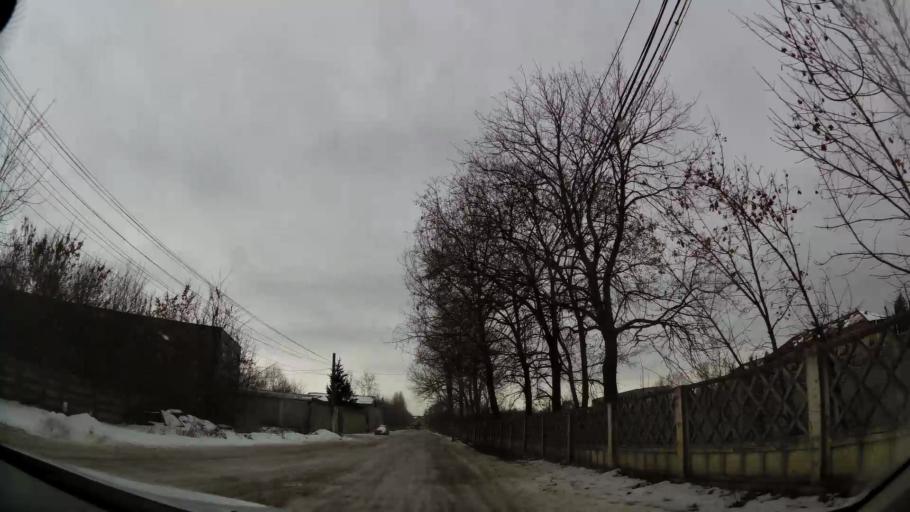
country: RO
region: Ilfov
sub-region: Comuna Pantelimon
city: Pantelimon
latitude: 44.4517
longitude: 26.2176
